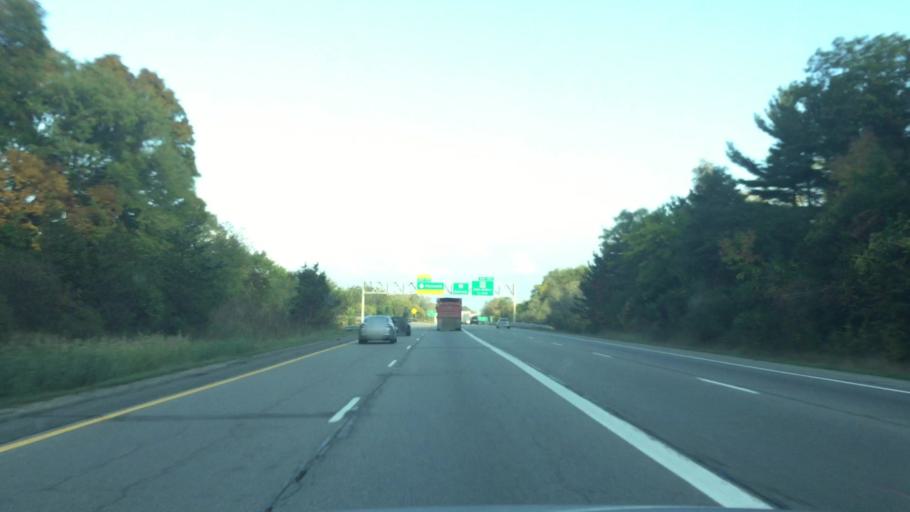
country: US
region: Michigan
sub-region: Washtenaw County
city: Ann Arbor
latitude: 42.2884
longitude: -83.8084
